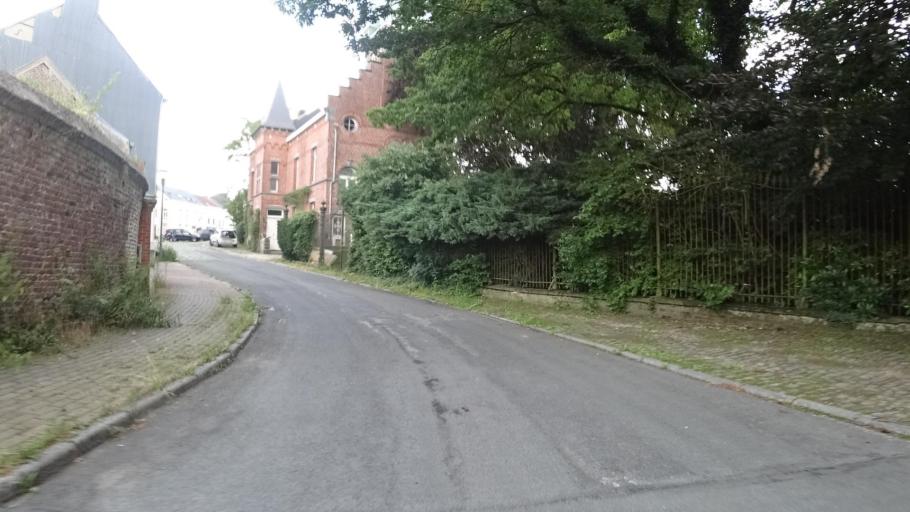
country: BE
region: Wallonia
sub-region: Province du Brabant Wallon
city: Villers-la-Ville
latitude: 50.5448
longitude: 4.5318
